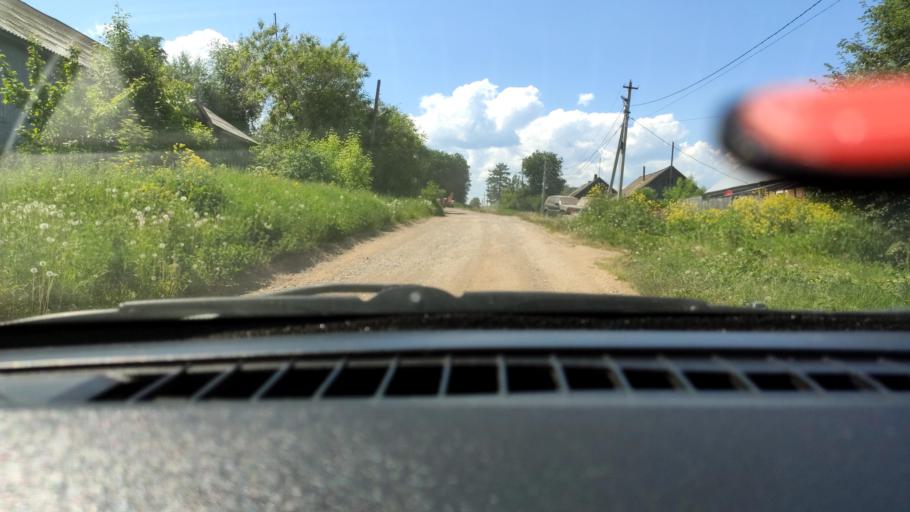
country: RU
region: Perm
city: Sylva
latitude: 58.0358
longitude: 56.7771
